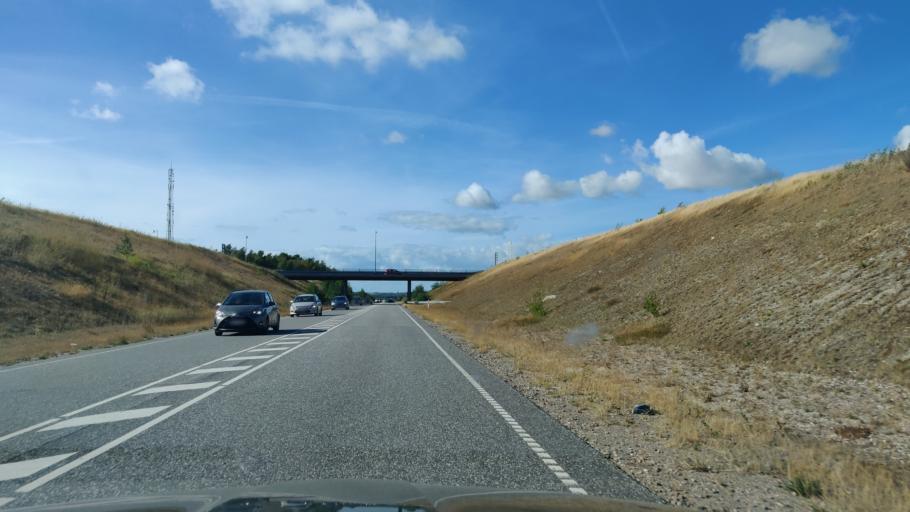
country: DK
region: Zealand
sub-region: Odsherred Kommune
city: Hojby
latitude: 55.8676
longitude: 11.5881
